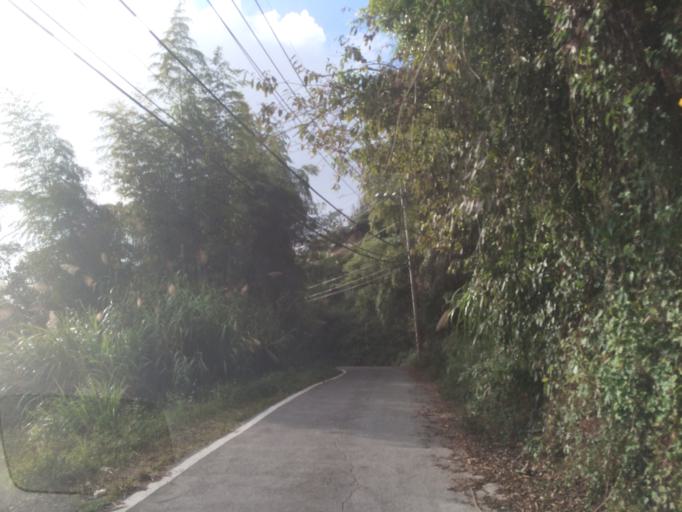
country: TW
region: Taiwan
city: Lugu
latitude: 23.6562
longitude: 120.7764
